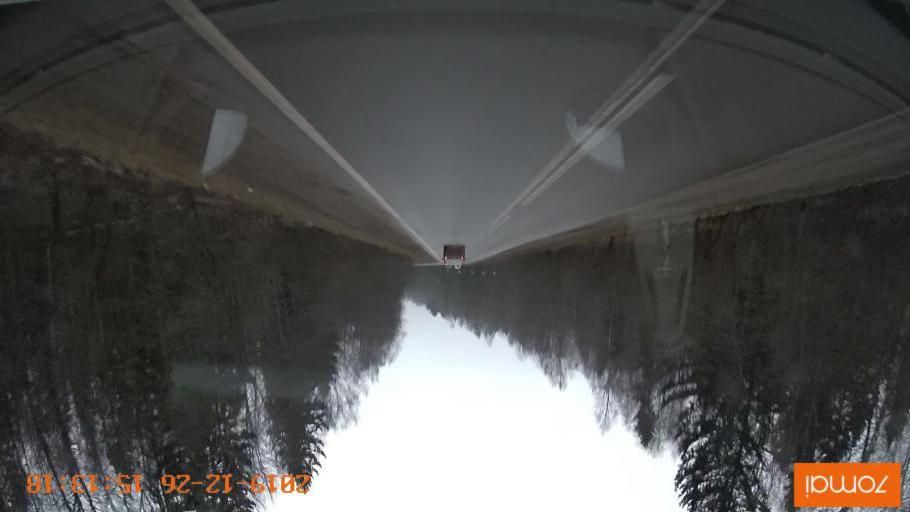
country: RU
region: Jaroslavl
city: Rybinsk
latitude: 58.1185
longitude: 38.8837
